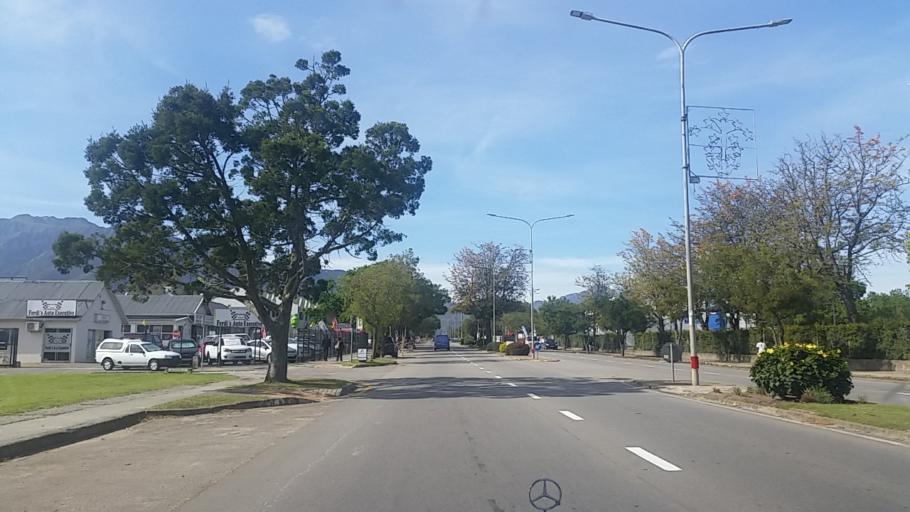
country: ZA
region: Western Cape
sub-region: Eden District Municipality
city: George
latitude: -33.9694
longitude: 22.4483
